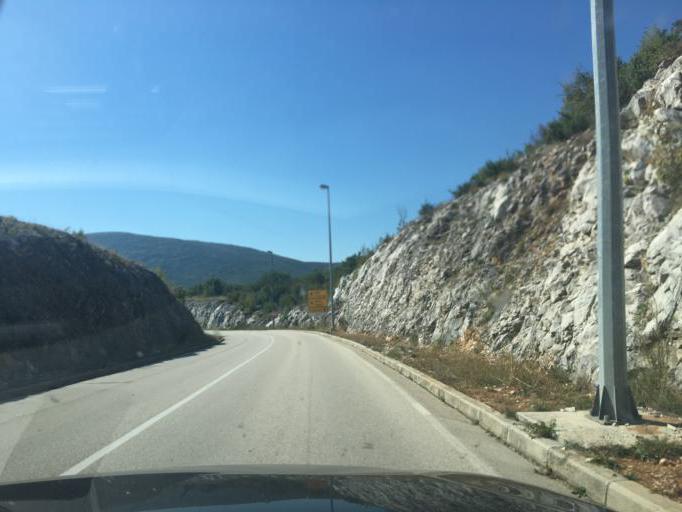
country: HR
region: Splitsko-Dalmatinska
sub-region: Grad Trogir
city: Trogir
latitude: 43.6102
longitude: 16.2237
